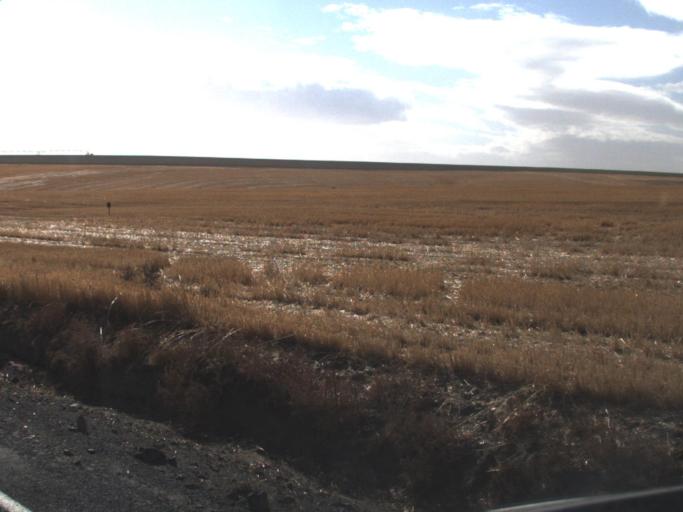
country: US
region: Washington
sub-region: Okanogan County
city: Coulee Dam
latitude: 47.5928
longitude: -118.7861
